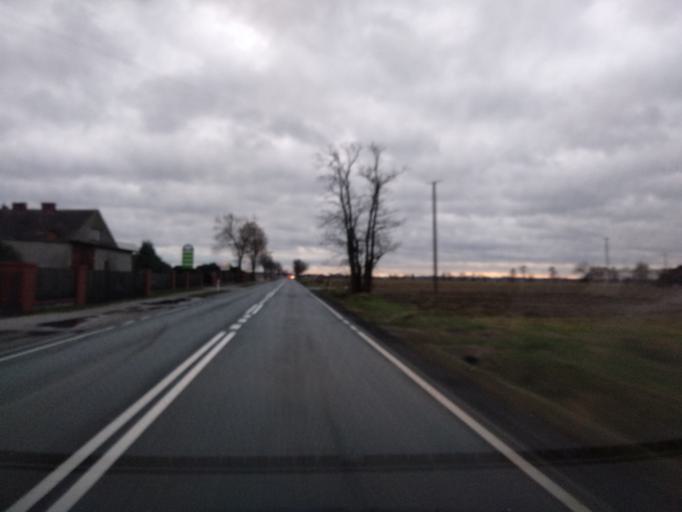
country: PL
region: Greater Poland Voivodeship
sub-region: Powiat koninski
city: Rychwal
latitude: 52.1157
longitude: 18.1676
